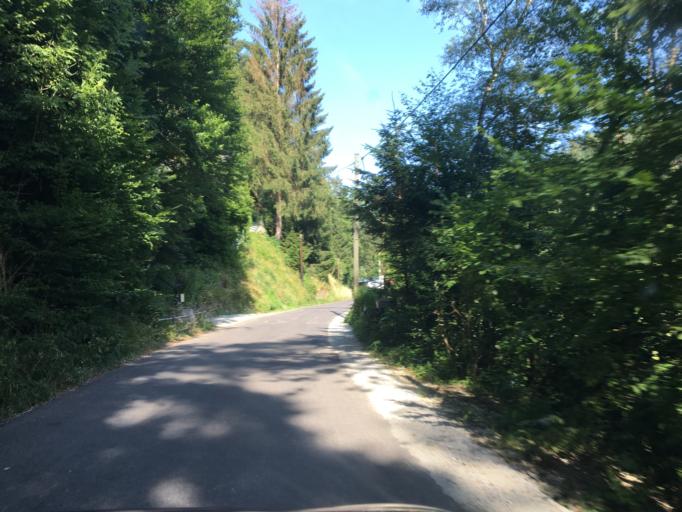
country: AT
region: Upper Austria
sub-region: Politischer Bezirk Urfahr-Umgebung
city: Walding
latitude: 48.3697
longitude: 14.1510
